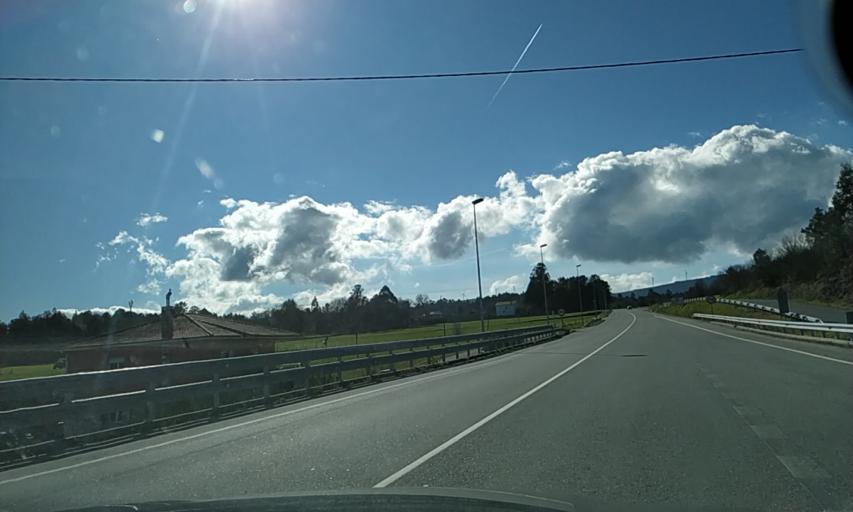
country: ES
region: Galicia
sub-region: Provincia de Pontevedra
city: Silleda
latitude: 42.7171
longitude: -8.2855
